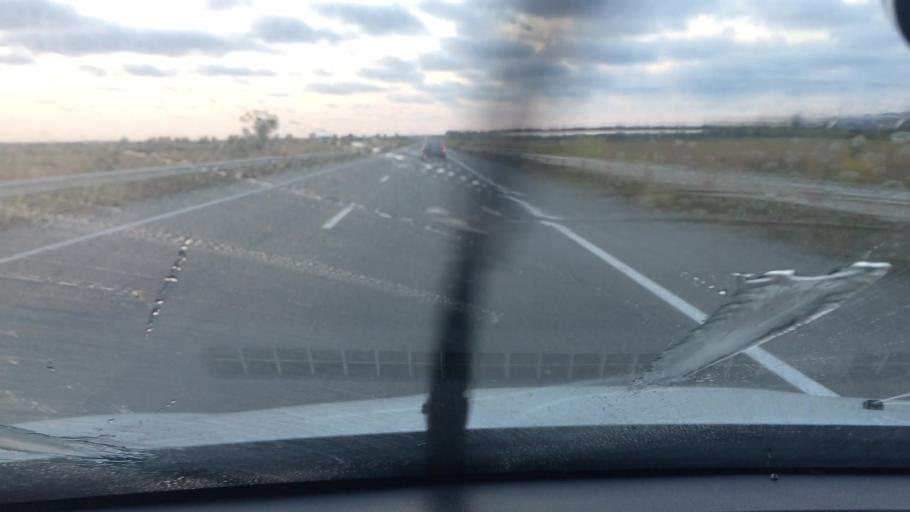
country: GE
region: Ajaria
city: Ochkhamuri
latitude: 41.8743
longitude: 41.8266
